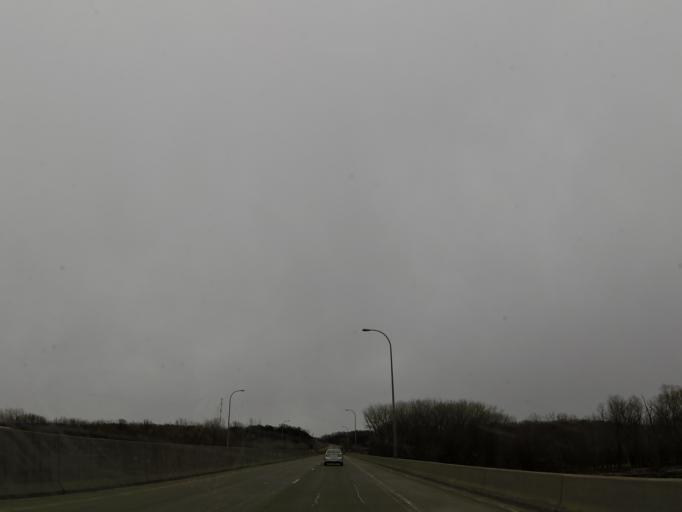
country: US
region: Minnesota
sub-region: Le Sueur County
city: Le Sueur
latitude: 44.4805
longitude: -93.9059
